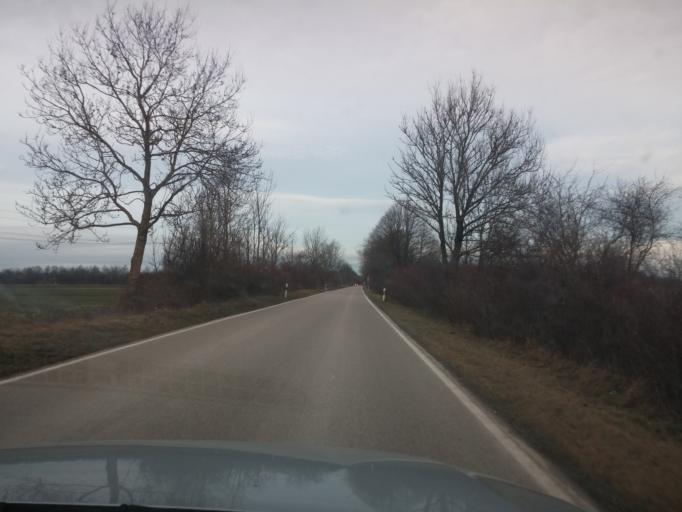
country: DE
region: Bavaria
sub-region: Upper Bavaria
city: Unterfoehring
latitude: 48.1849
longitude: 11.6734
